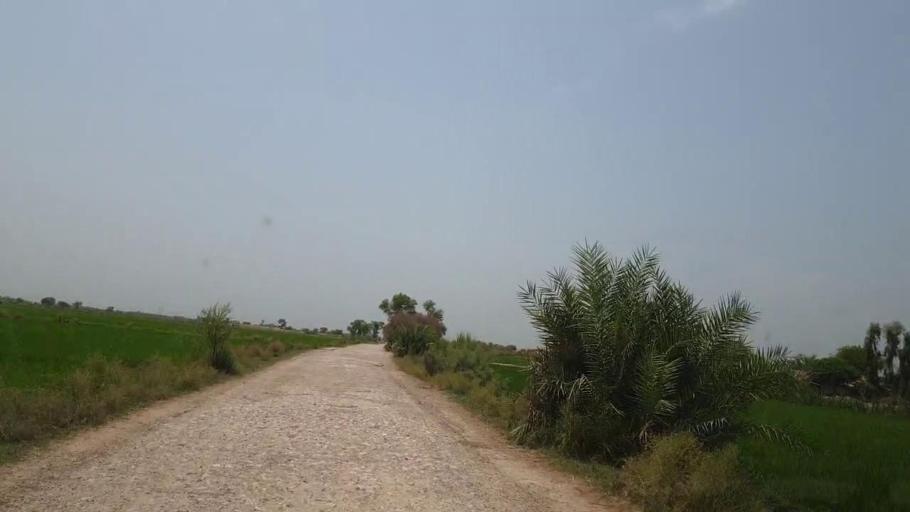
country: PK
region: Sindh
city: Shikarpur
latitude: 27.9096
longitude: 68.6340
